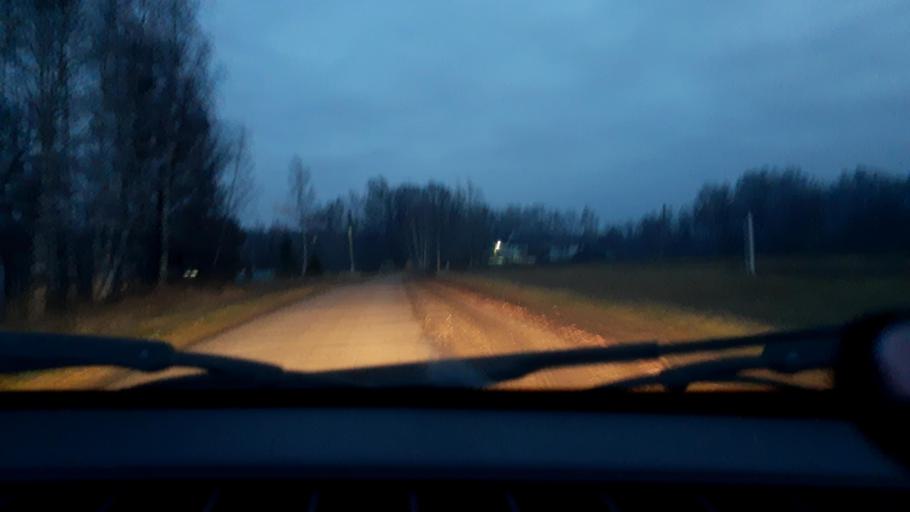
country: RU
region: Bashkortostan
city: Mikhaylovka
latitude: 54.8301
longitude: 55.8540
